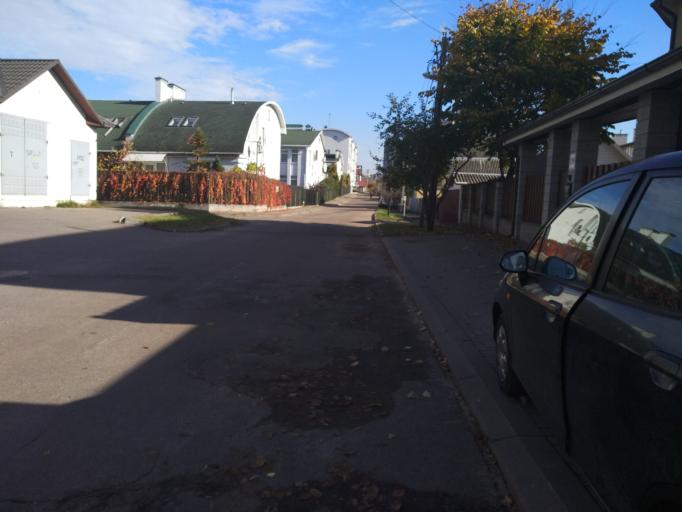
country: BY
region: Minsk
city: Minsk
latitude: 53.9406
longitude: 27.5737
